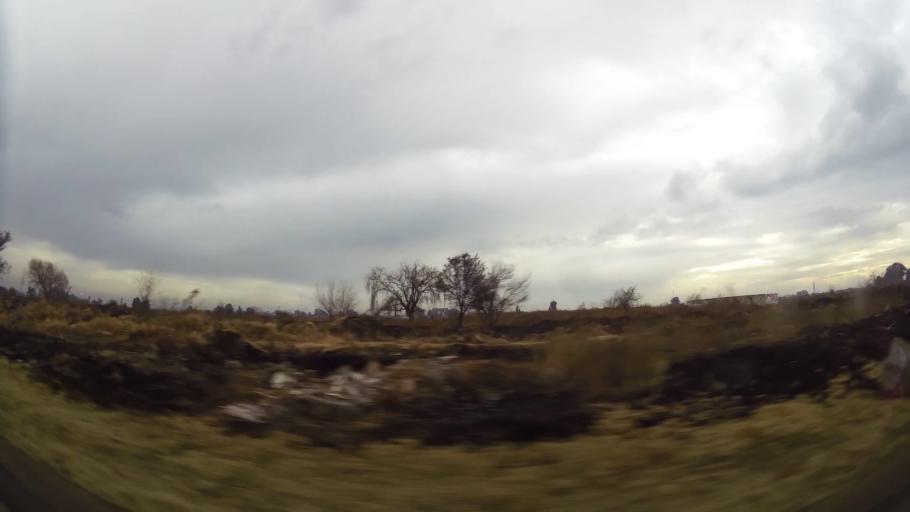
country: ZA
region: Gauteng
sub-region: Ekurhuleni Metropolitan Municipality
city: Germiston
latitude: -26.3372
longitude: 28.1902
